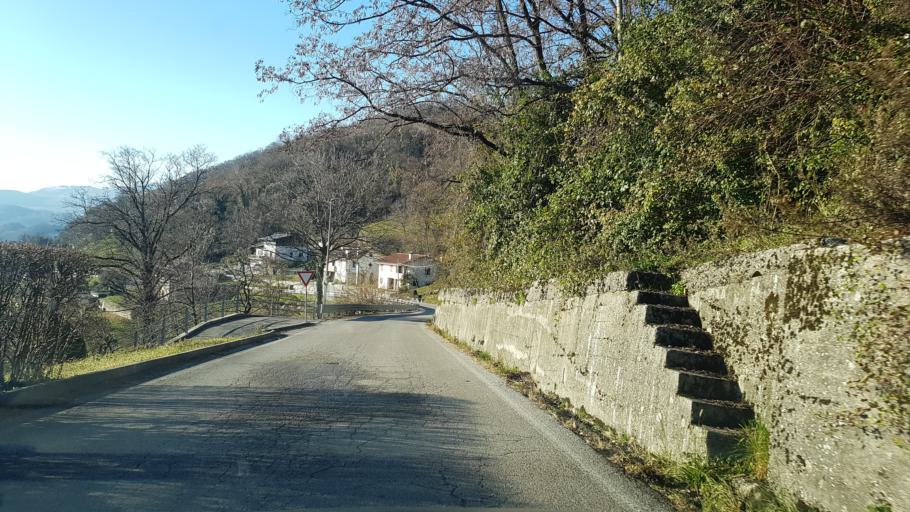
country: IT
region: Friuli Venezia Giulia
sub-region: Provincia di Udine
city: Forgaria nel Friuli
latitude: 46.2260
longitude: 12.9861
